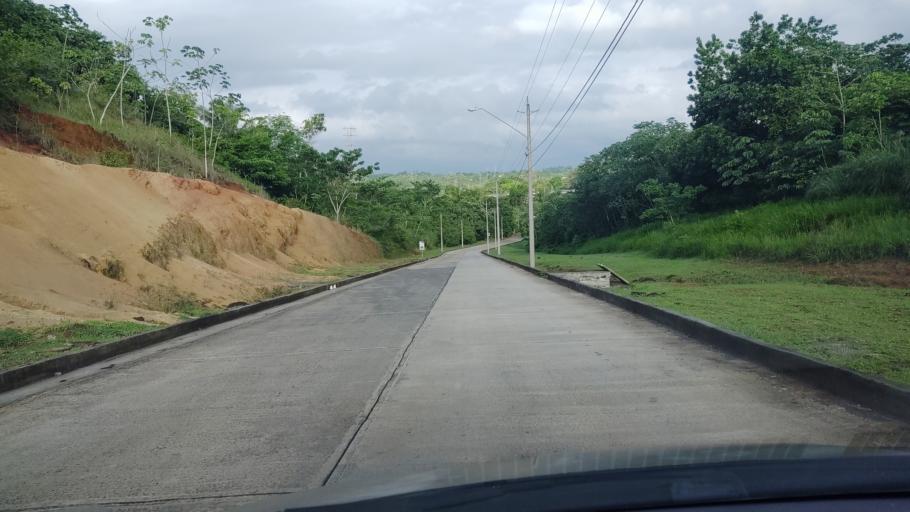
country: PA
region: Panama
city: Nuevo Arraijan
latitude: 8.9257
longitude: -79.7573
